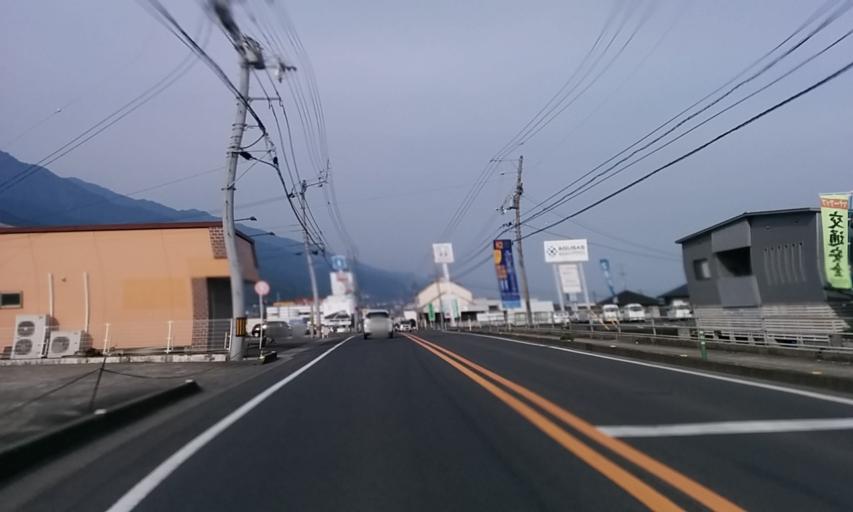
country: JP
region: Ehime
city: Kawanoecho
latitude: 33.9698
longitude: 133.5205
